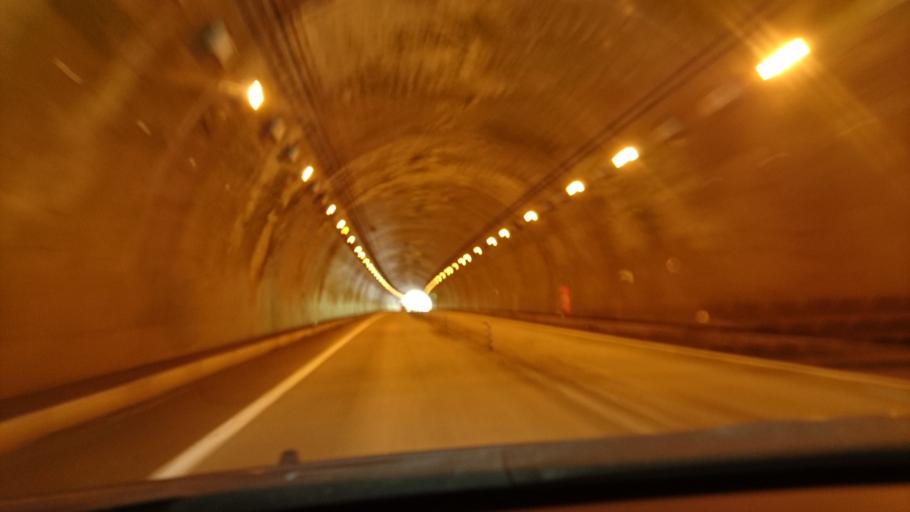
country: JP
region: Iwate
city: Ofunato
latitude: 39.0791
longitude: 141.7012
